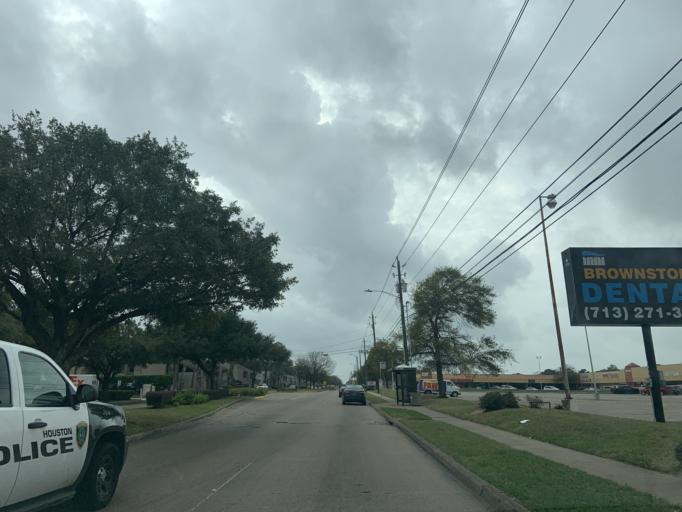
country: US
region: Texas
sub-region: Harris County
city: Bellaire
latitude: 29.6741
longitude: -95.5088
